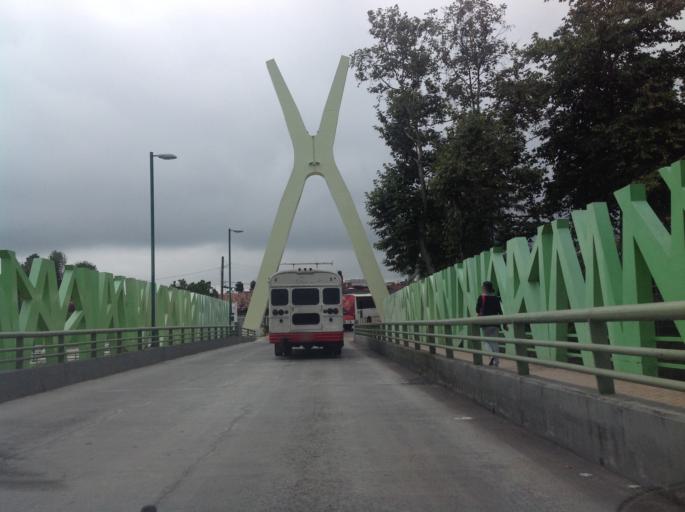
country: MX
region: Veracruz
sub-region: Xalapa
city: Xalapa de Enriquez
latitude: 19.5188
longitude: -96.9217
